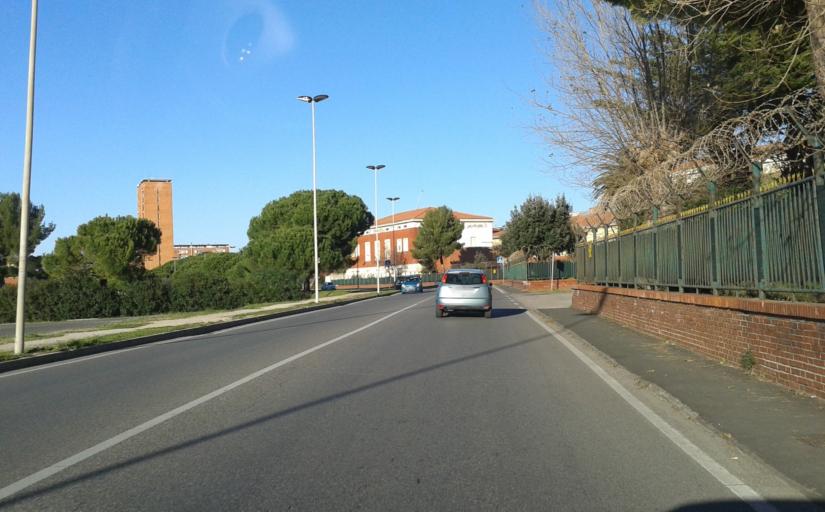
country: IT
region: Tuscany
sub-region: Provincia di Livorno
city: Livorno
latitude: 43.5196
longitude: 10.3241
